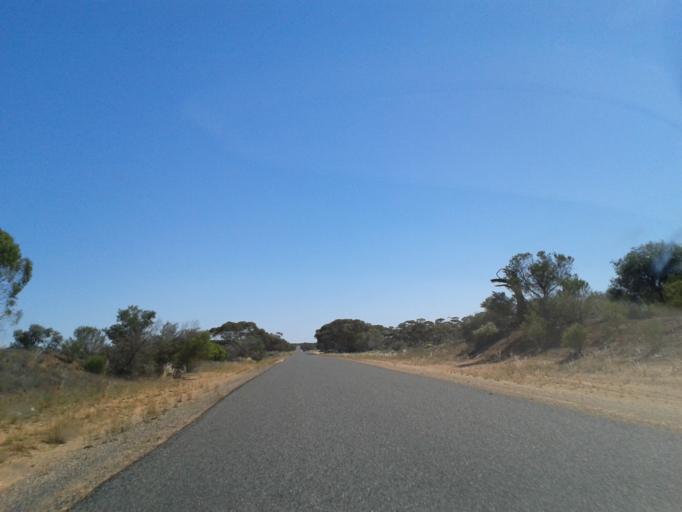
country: AU
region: New South Wales
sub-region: Wentworth
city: Dareton
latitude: -34.1759
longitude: 141.9970
